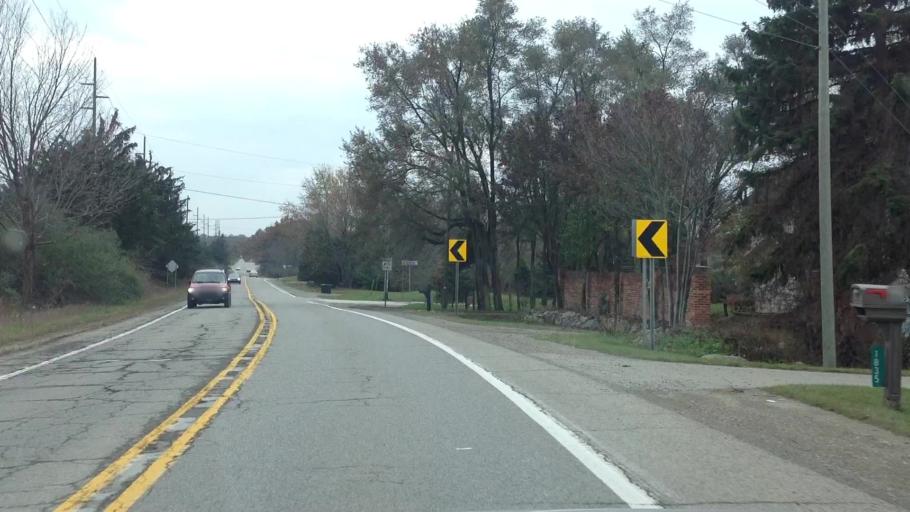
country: US
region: Michigan
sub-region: Oakland County
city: Milford
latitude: 42.6057
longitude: -83.6610
